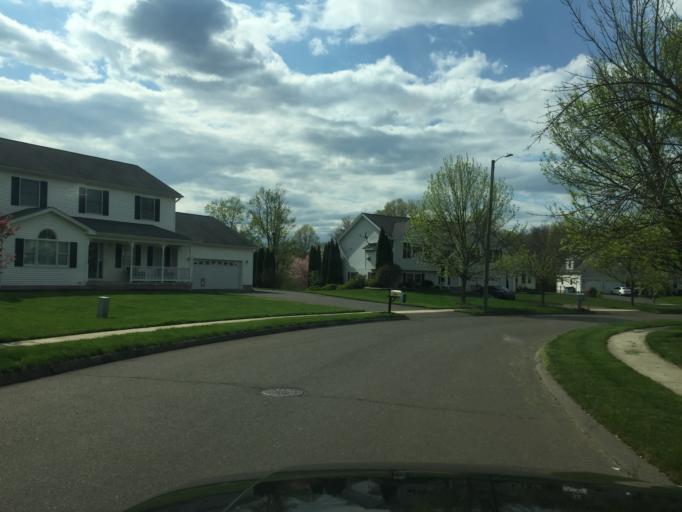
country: US
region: Connecticut
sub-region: Hartford County
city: Kensington
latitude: 41.6222
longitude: -72.7572
